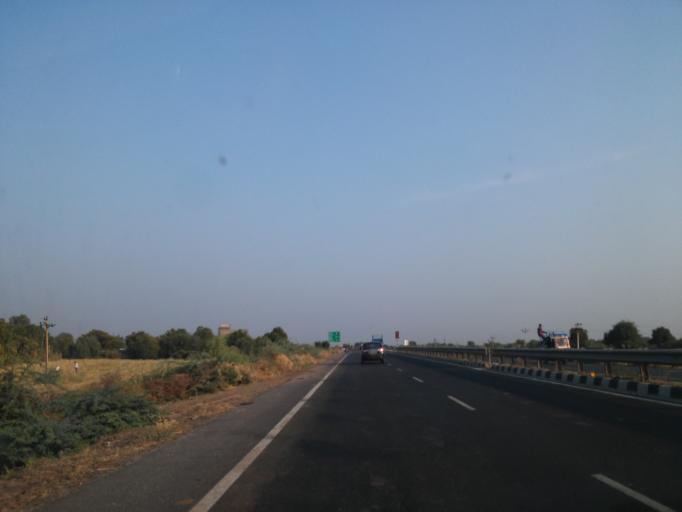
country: IN
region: Gujarat
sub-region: Ahmadabad
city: Sanand
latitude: 23.0774
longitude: 72.1721
